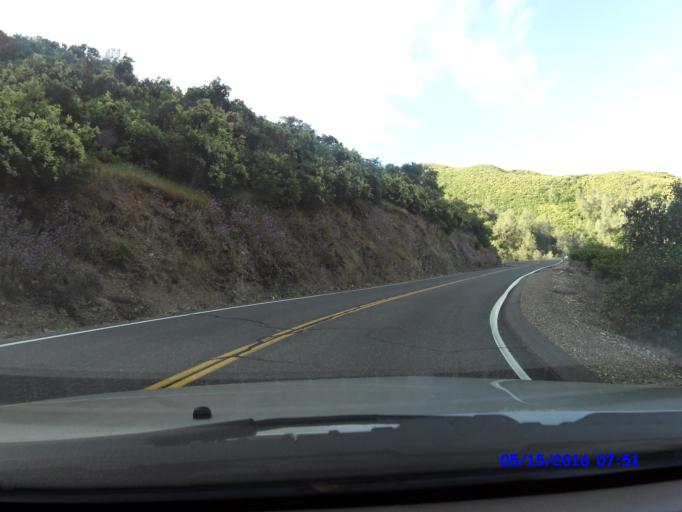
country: US
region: California
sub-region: Mariposa County
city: Mariposa
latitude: 37.5967
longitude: -120.1304
